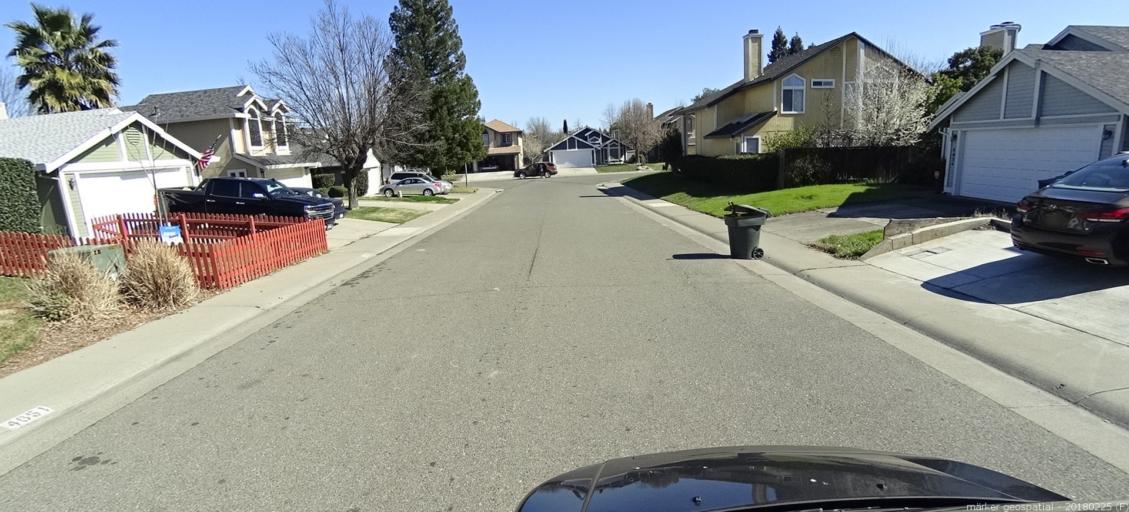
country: US
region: California
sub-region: Sacramento County
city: Antelope
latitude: 38.7250
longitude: -121.3553
